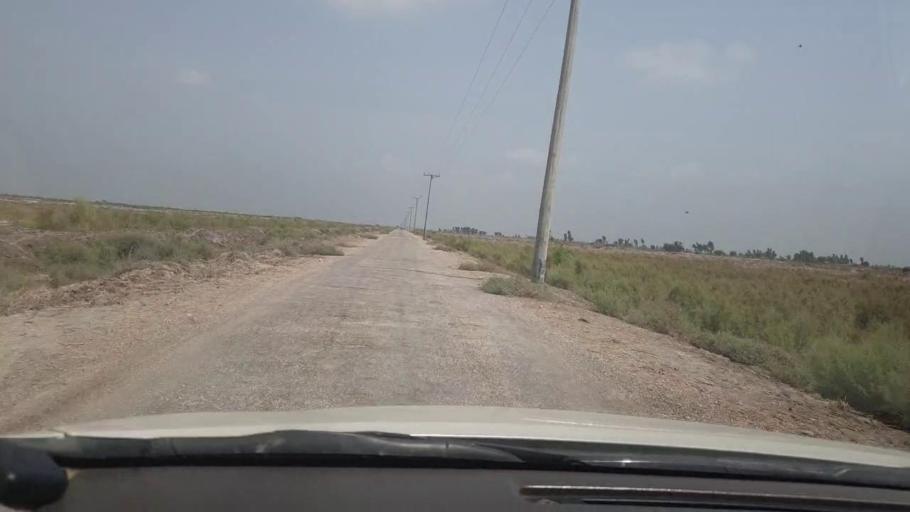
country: PK
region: Sindh
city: Garhi Yasin
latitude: 27.9914
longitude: 68.5014
